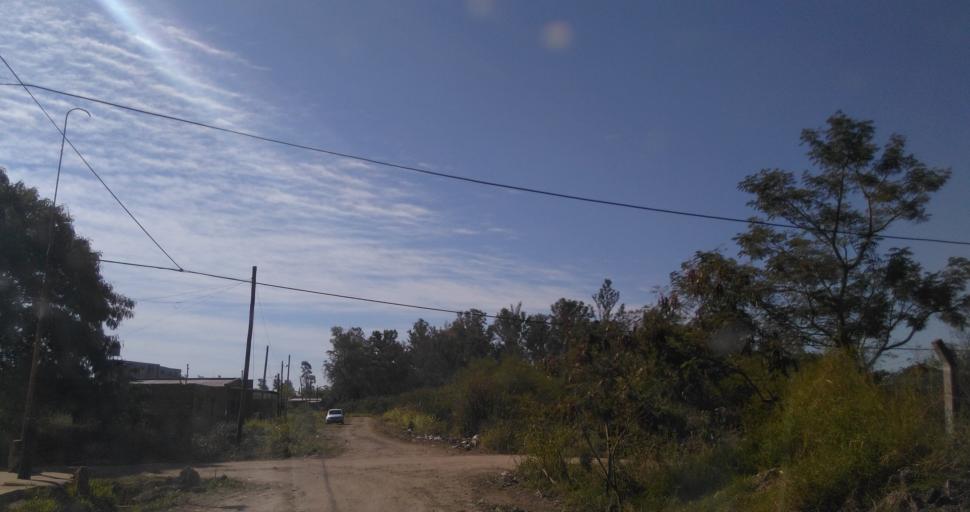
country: AR
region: Chaco
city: Fontana
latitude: -27.4479
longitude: -59.0307
